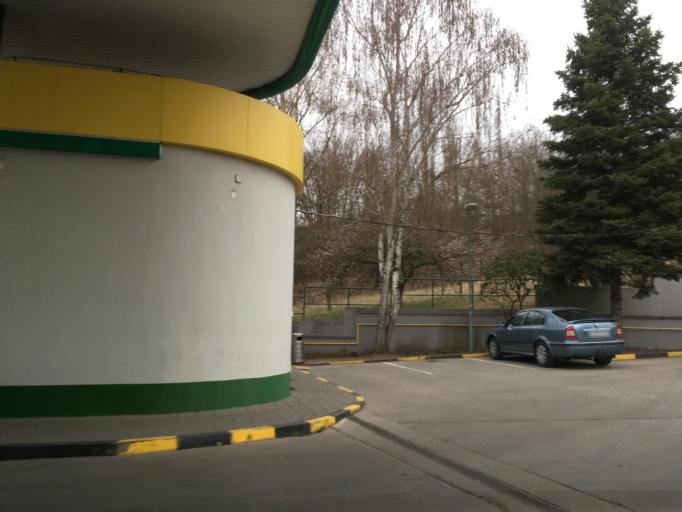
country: SK
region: Nitriansky
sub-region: Okres Nove Zamky
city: Sturovo
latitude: 47.7890
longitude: 18.7108
